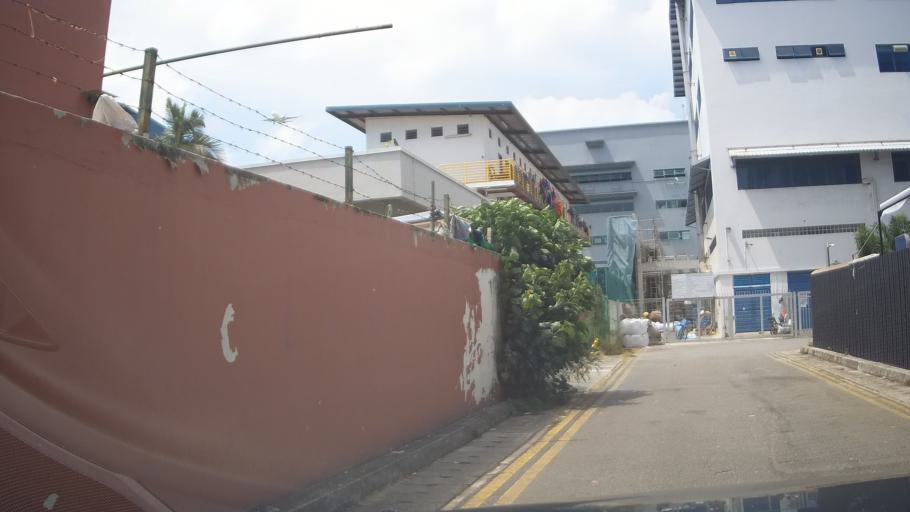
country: SG
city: Singapore
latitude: 1.3324
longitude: 103.9688
